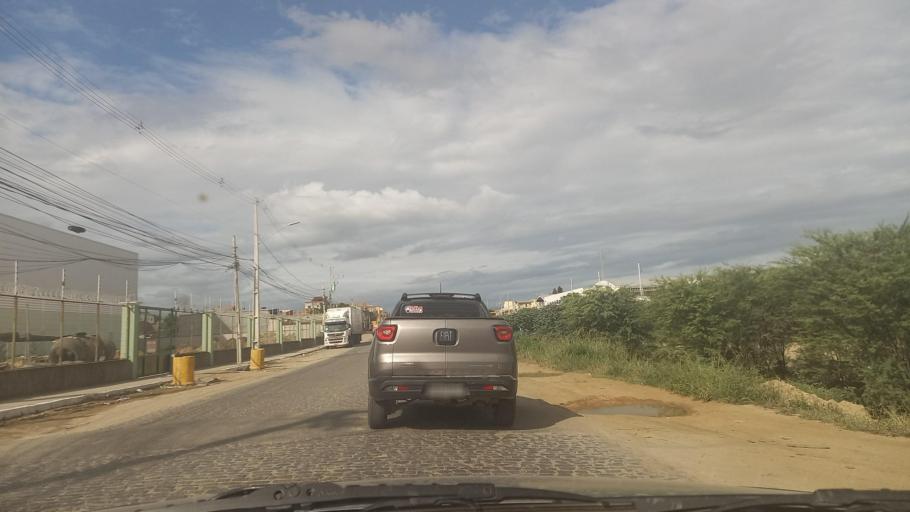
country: BR
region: Pernambuco
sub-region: Caruaru
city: Caruaru
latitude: -8.2885
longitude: -36.0097
